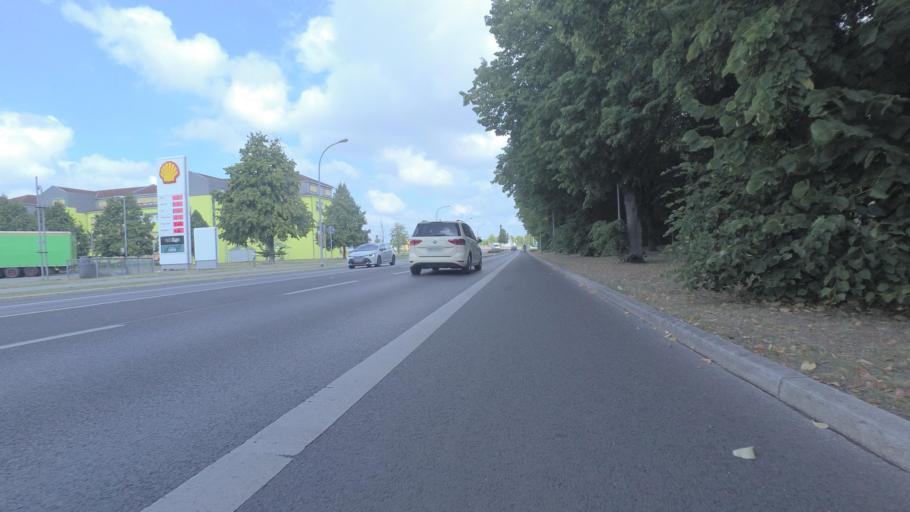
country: DE
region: Brandenburg
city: Neuruppin
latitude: 52.9184
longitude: 12.7895
